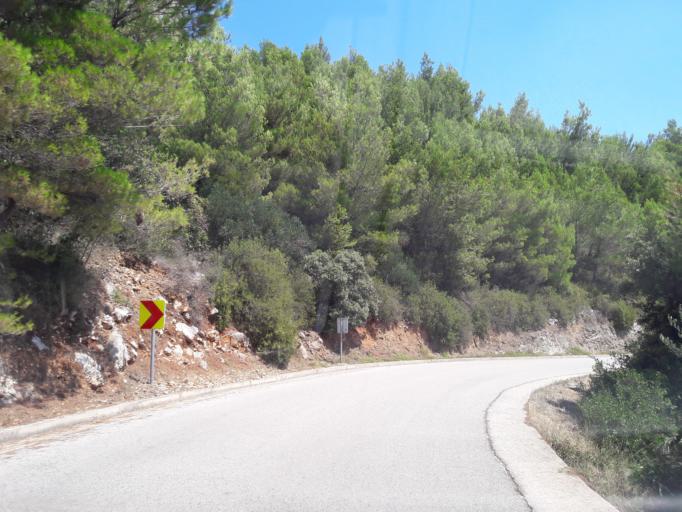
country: HR
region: Dubrovacko-Neretvanska
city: Blato
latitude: 42.9060
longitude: 17.4250
